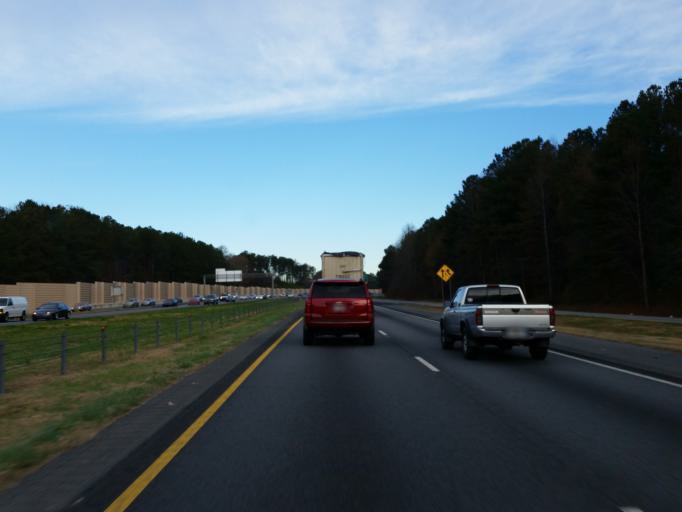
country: US
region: Georgia
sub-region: Cherokee County
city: Woodstock
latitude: 34.1055
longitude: -84.5321
